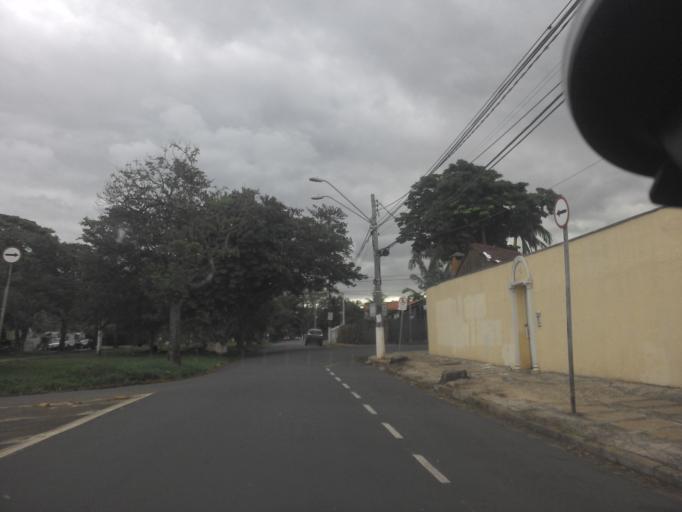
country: BR
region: Sao Paulo
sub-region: Campinas
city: Campinas
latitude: -22.8193
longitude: -47.0741
